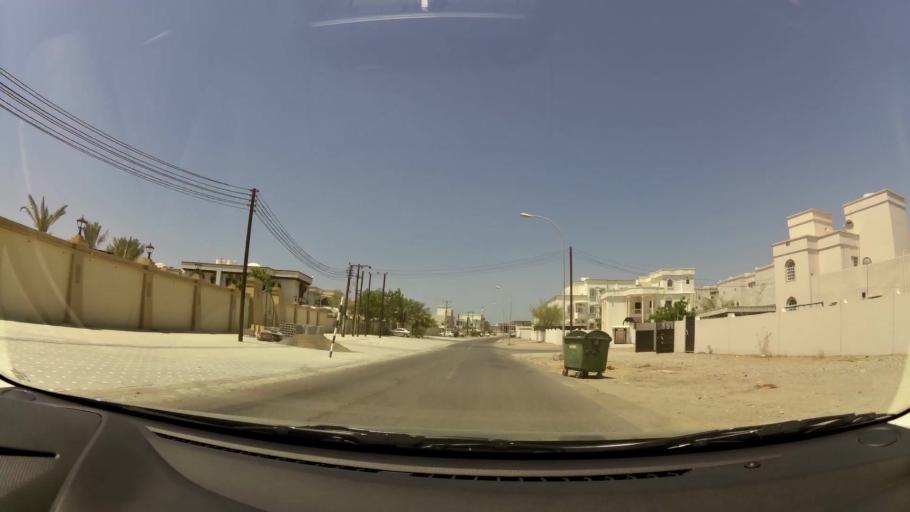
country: OM
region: Muhafazat Masqat
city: As Sib al Jadidah
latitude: 23.6190
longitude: 58.2349
